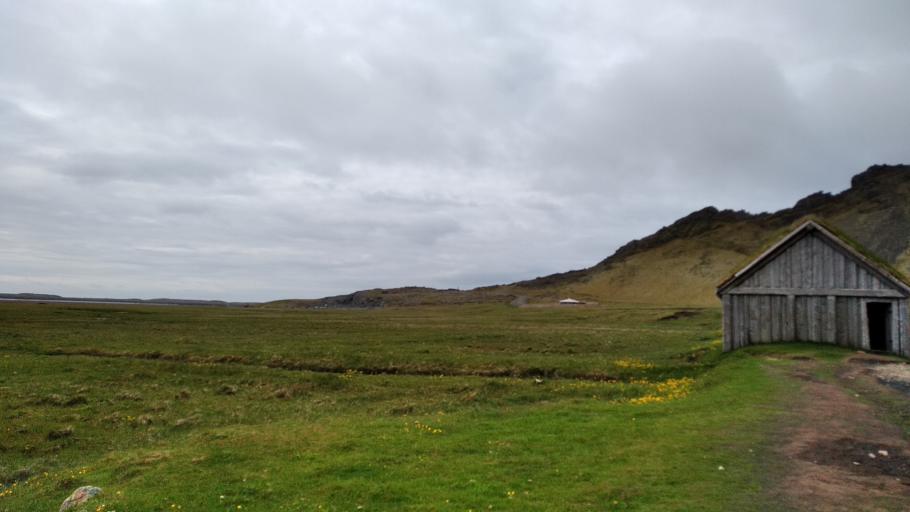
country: IS
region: East
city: Hoefn
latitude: 64.2603
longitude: -14.9864
